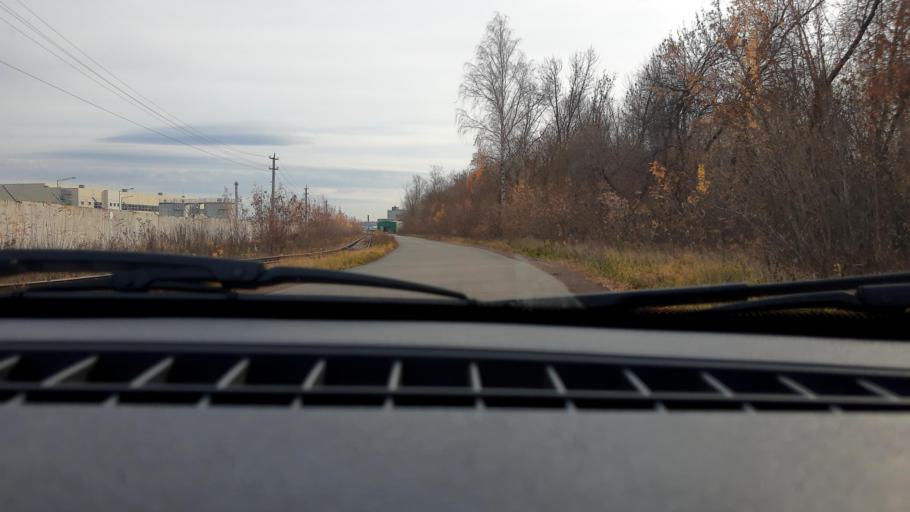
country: RU
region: Bashkortostan
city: Ufa
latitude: 54.5902
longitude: 55.9021
